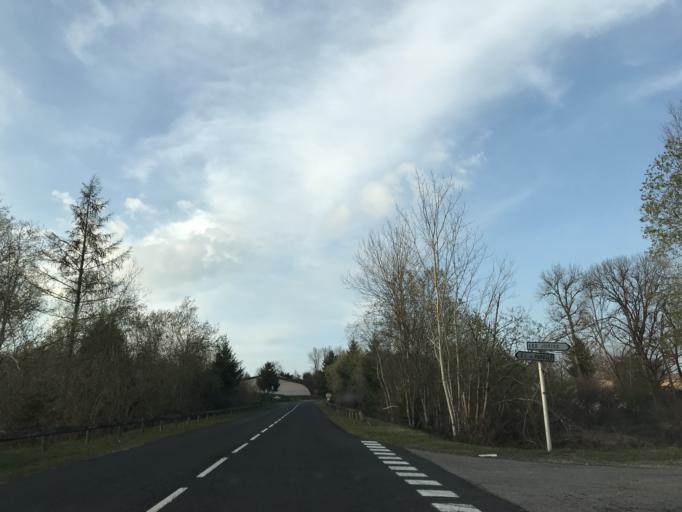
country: FR
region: Auvergne
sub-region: Departement du Puy-de-Dome
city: Saint-Remy-sur-Durolle
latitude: 45.8767
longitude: 3.5914
